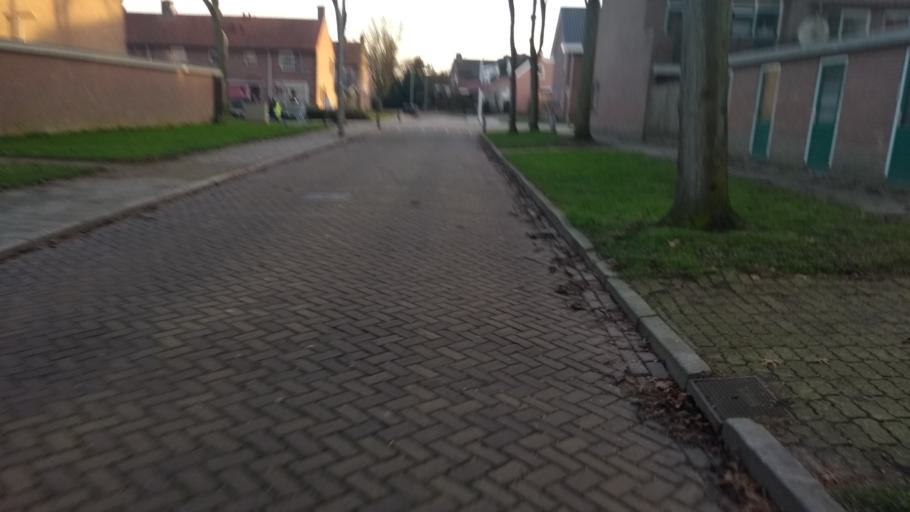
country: NL
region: Overijssel
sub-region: Gemeente Almelo
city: Almelo
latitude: 52.3674
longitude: 6.6741
